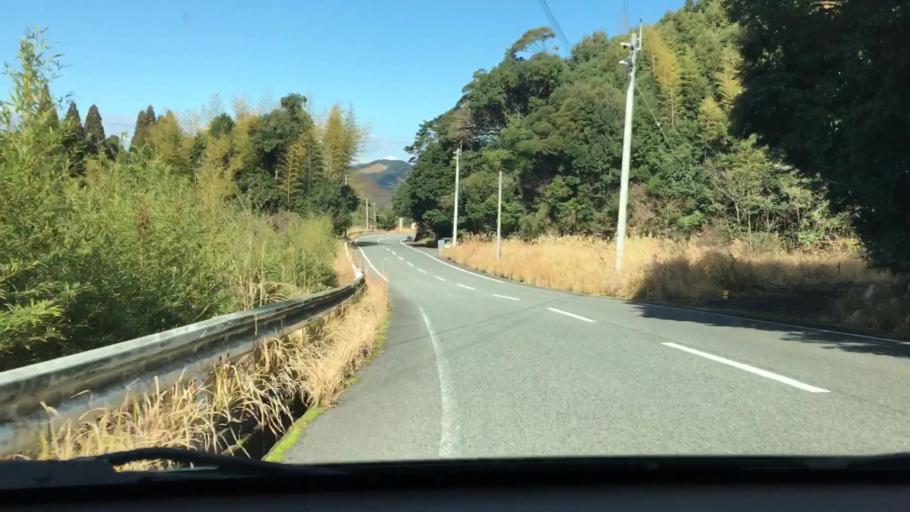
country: JP
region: Kagoshima
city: Ijuin
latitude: 31.7196
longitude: 130.4159
